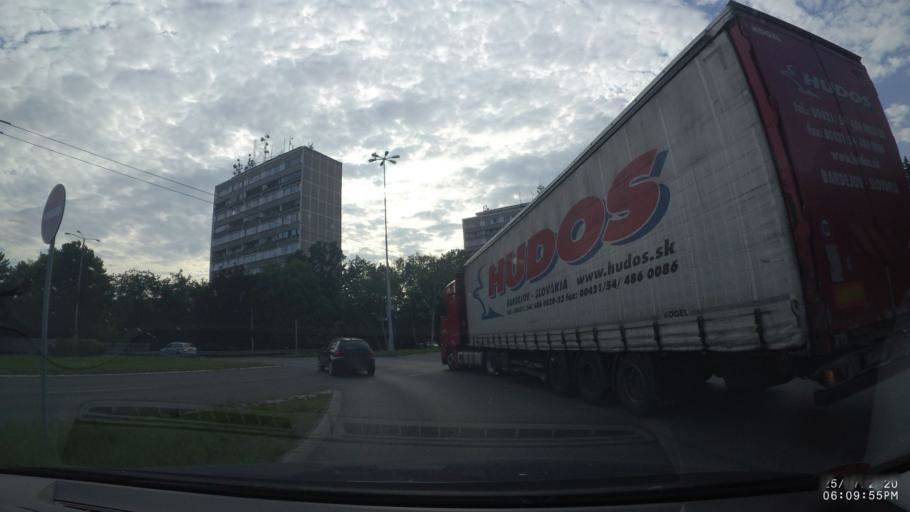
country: CZ
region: Kralovehradecky
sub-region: Okres Hradec Kralove
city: Hradec Kralove
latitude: 50.2031
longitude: 15.8216
